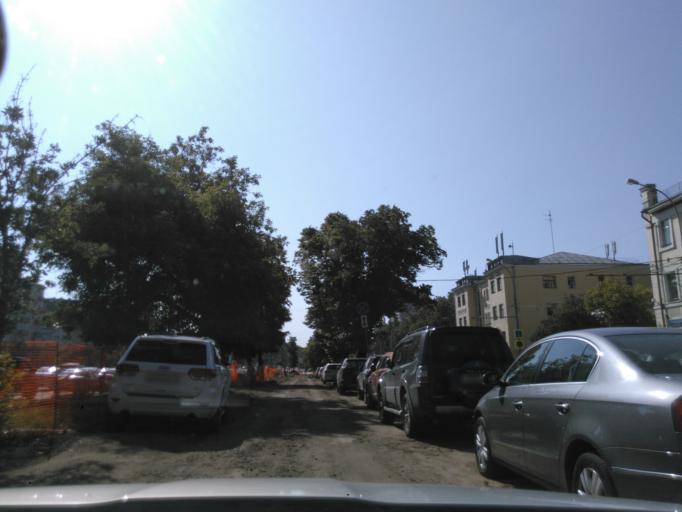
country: RU
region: Moskovskaya
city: Dorogomilovo
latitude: 55.7799
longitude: 37.5772
